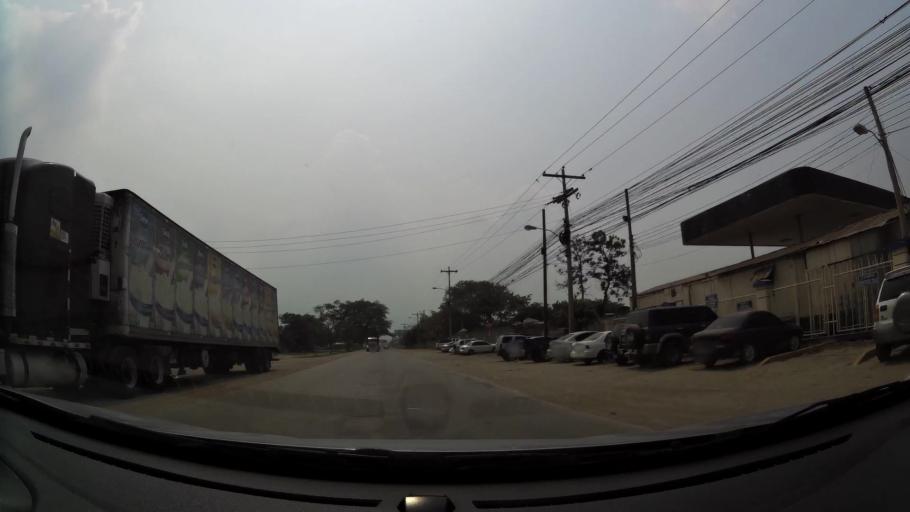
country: HN
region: Cortes
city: Chotepe
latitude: 15.4682
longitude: -87.9850
